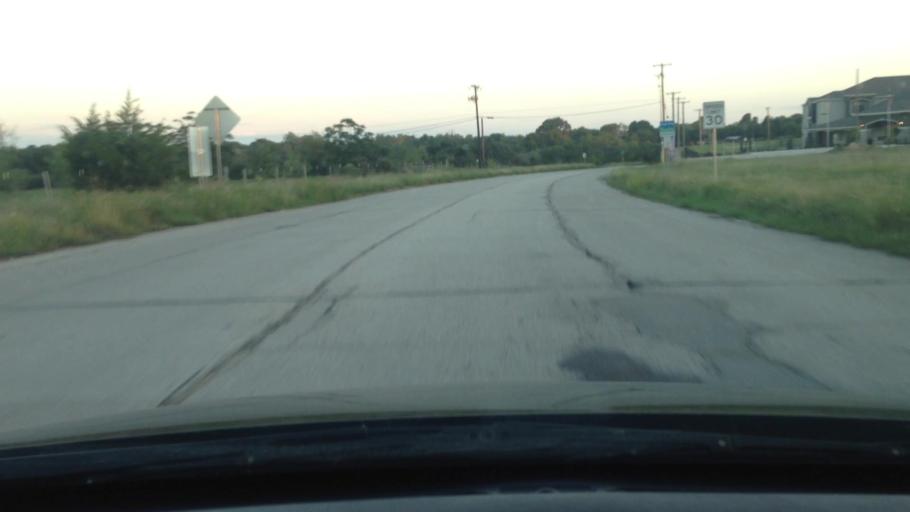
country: US
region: Texas
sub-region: Tarrant County
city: White Settlement
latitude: 32.7812
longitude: -97.4671
